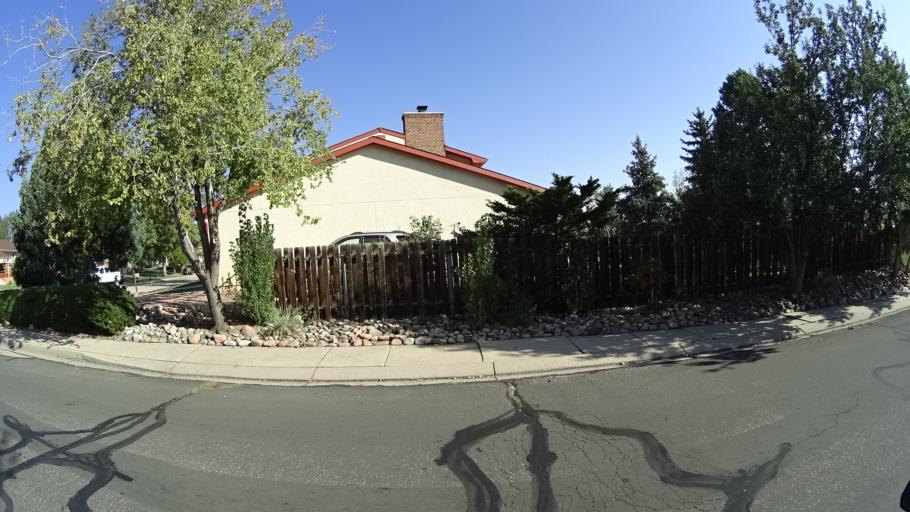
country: US
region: Colorado
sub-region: El Paso County
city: Cimarron Hills
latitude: 38.8809
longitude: -104.7278
